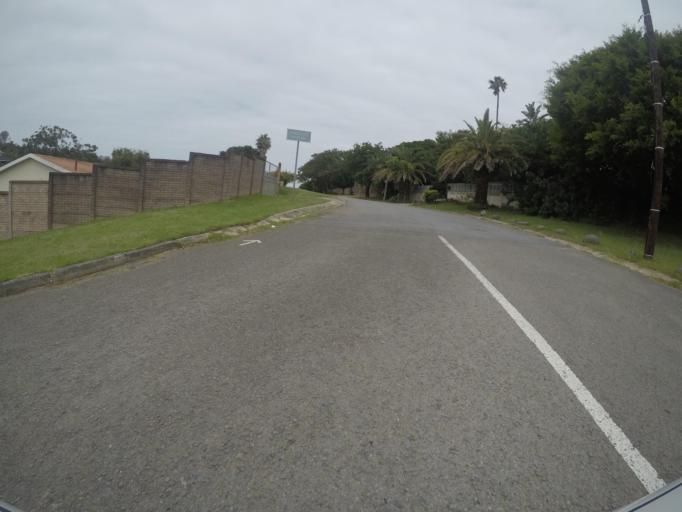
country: ZA
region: Eastern Cape
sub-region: Buffalo City Metropolitan Municipality
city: East London
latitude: -32.9738
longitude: 27.9461
